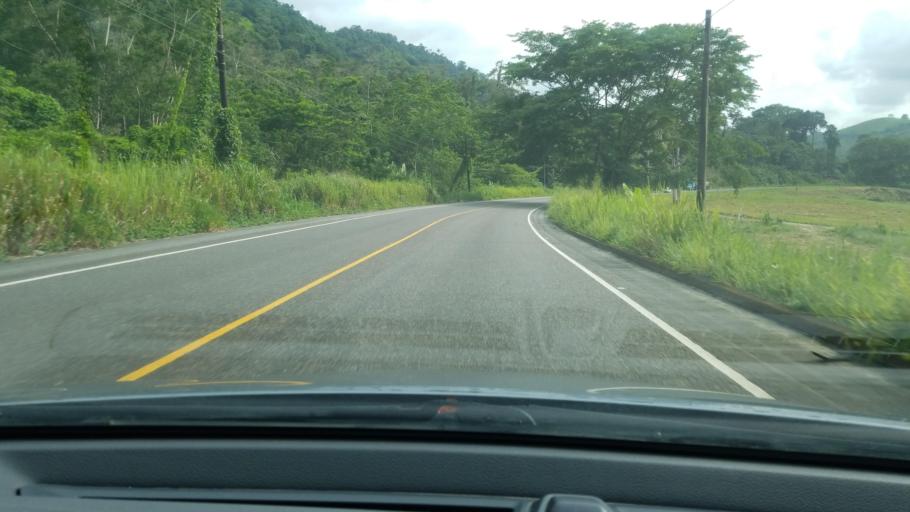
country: HN
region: Cortes
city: Potrerillos
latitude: 15.5969
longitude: -88.2999
